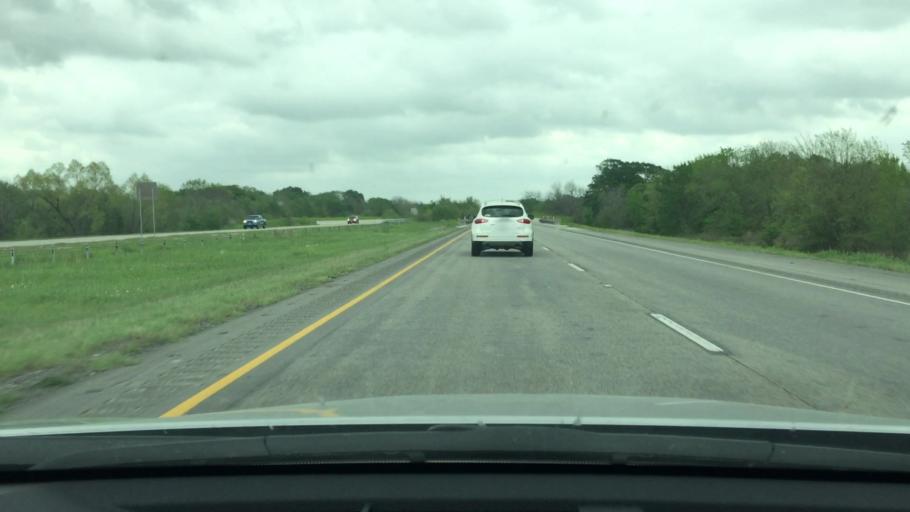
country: US
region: Texas
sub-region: Gonzales County
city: Waelder
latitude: 29.6924
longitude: -97.2377
